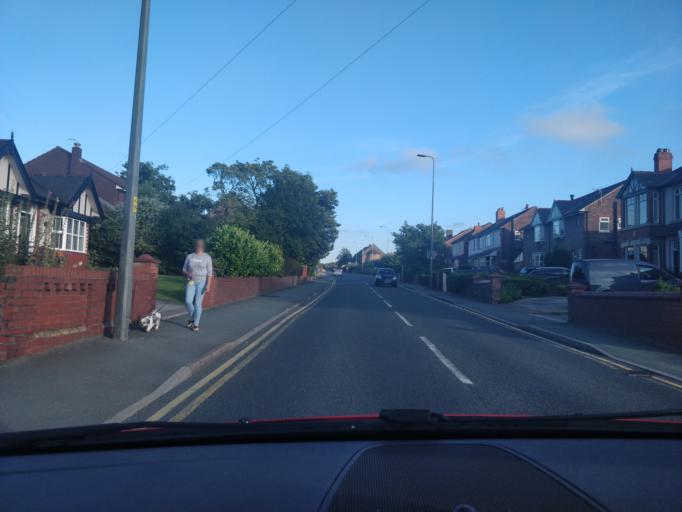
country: GB
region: England
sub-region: St. Helens
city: Billinge
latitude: 53.5215
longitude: -2.7154
